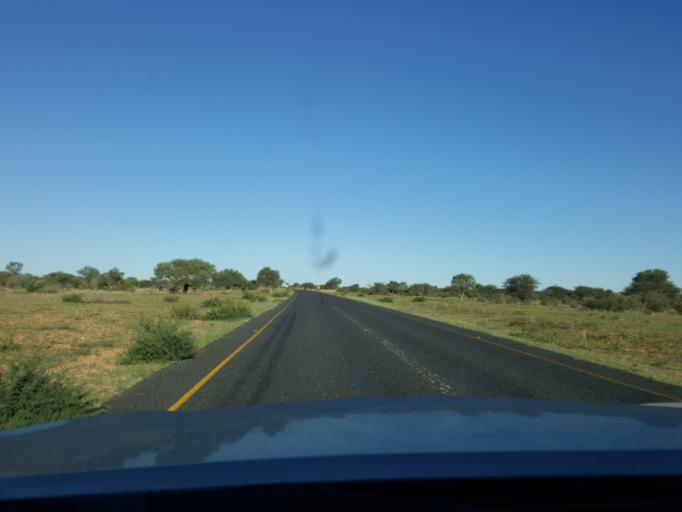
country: BW
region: Southern
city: Khakhea
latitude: -24.2274
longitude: 23.2415
